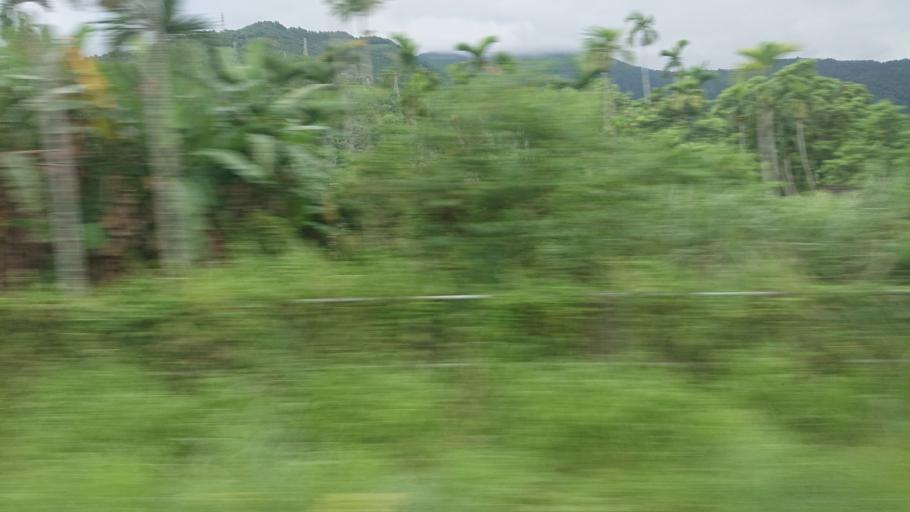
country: TW
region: Taiwan
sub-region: Hualien
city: Hualian
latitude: 23.6485
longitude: 121.4158
